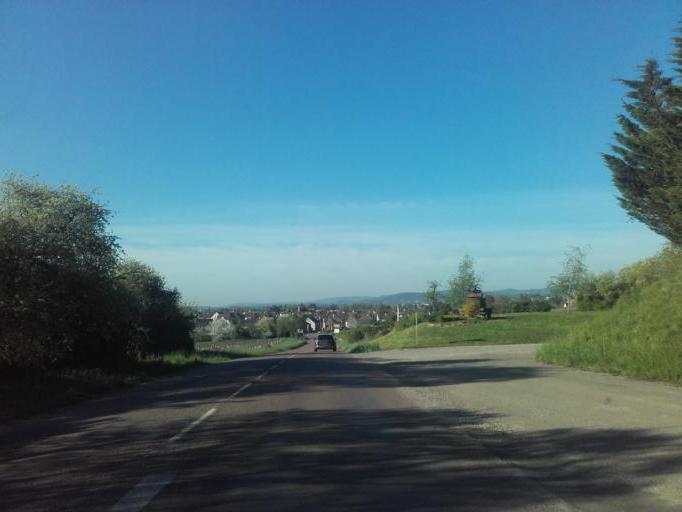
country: FR
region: Bourgogne
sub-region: Departement de Saone-et-Loire
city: Givry
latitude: 46.7895
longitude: 4.7469
